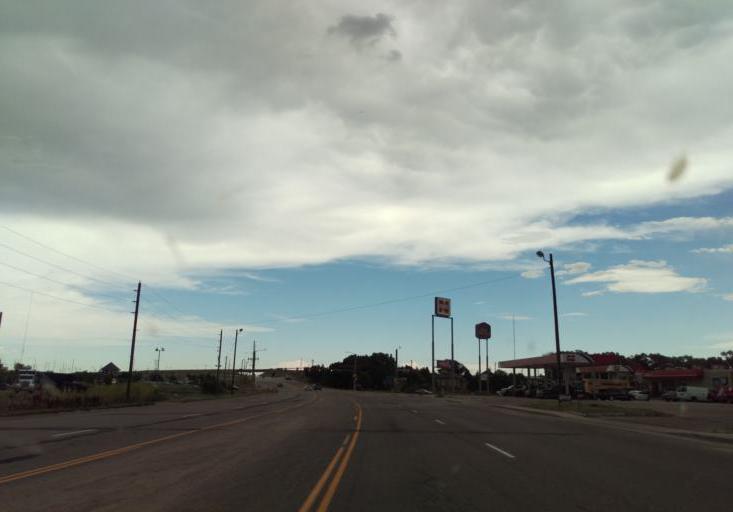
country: US
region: Colorado
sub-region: Logan County
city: Sterling
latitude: 40.6184
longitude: -103.1841
